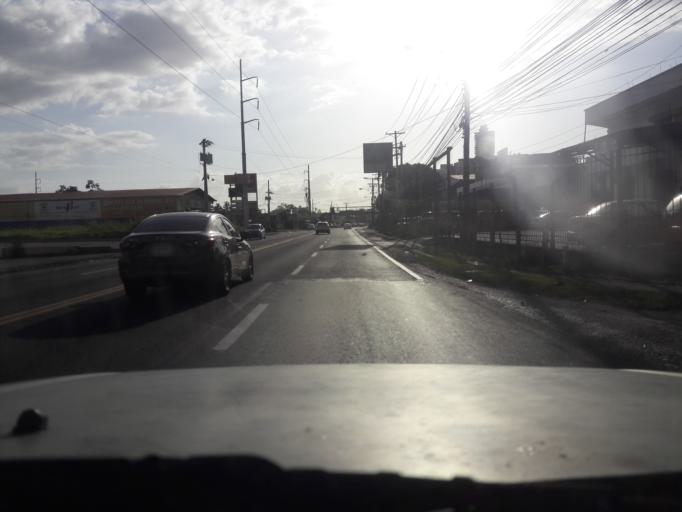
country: PA
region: Panama
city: San Miguelito
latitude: 9.0286
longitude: -79.4792
